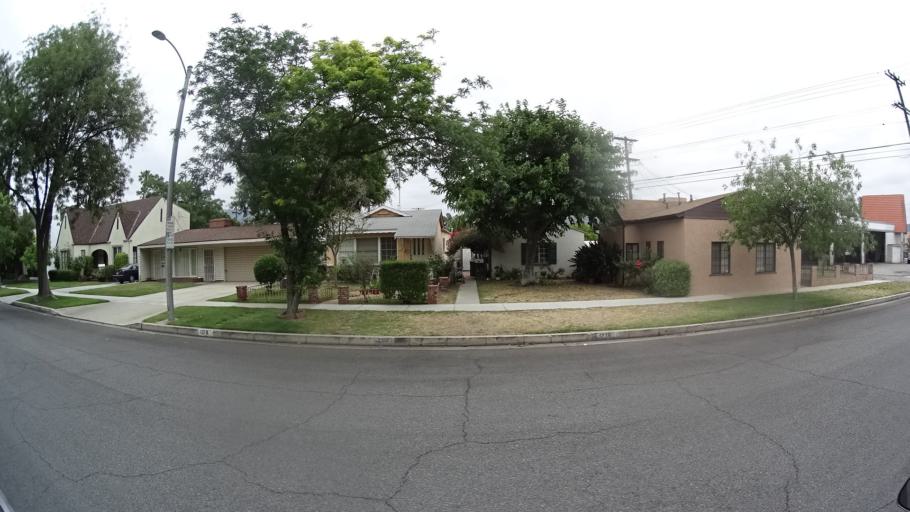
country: US
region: California
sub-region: Los Angeles County
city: Burbank
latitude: 34.1802
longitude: -118.3361
